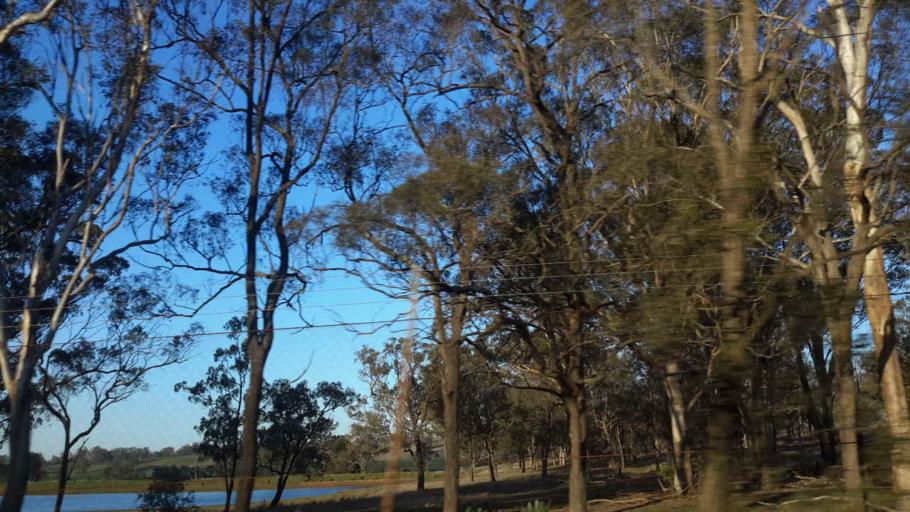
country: AU
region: New South Wales
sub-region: Camden
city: Camden South
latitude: -34.1282
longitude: 150.7028
